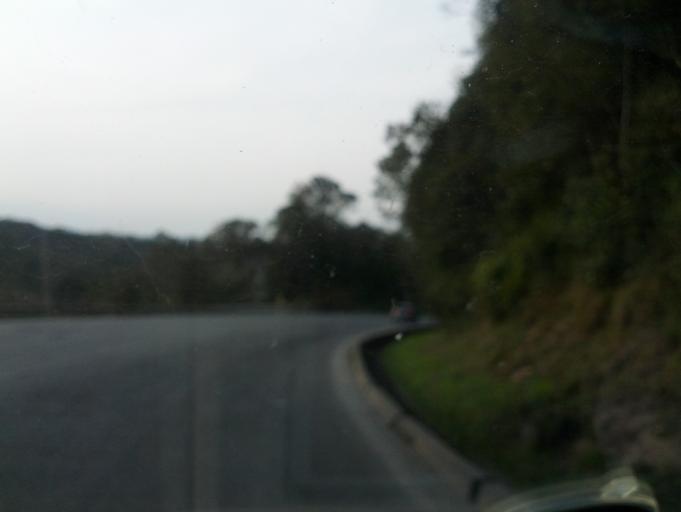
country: BR
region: Santa Catarina
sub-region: Otacilio Costa
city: Otacilio Costa
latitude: -27.2934
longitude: -50.0788
